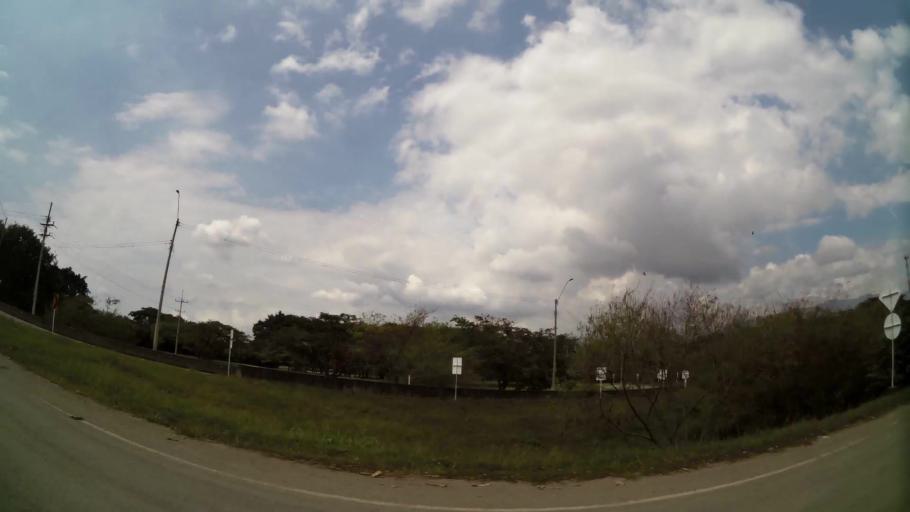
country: CO
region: Valle del Cauca
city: Cali
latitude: 3.4956
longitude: -76.4702
